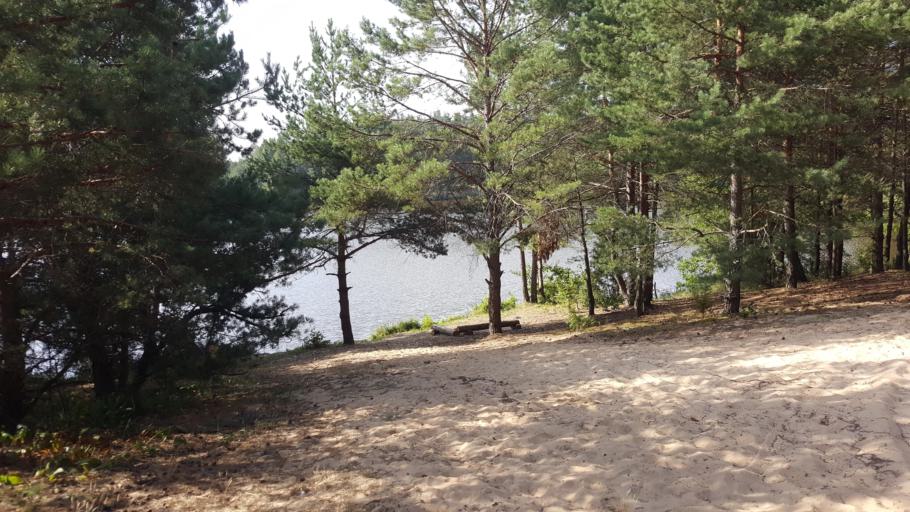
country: BY
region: Brest
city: Ivatsevichy
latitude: 52.7940
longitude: 25.5565
